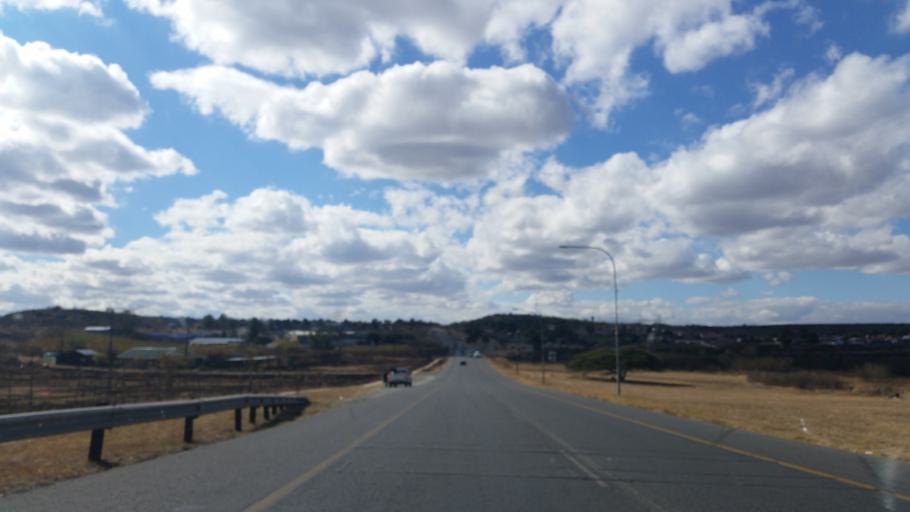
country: ZA
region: KwaZulu-Natal
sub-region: uThukela District Municipality
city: Ladysmith
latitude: -28.5401
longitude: 29.7964
